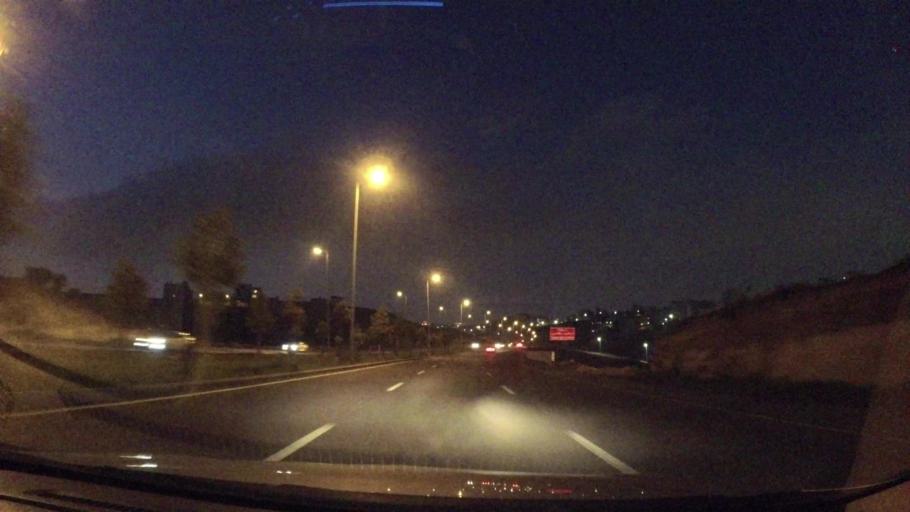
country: JO
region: Amman
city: Al Bunayyat ash Shamaliyah
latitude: 31.9154
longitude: 35.8794
